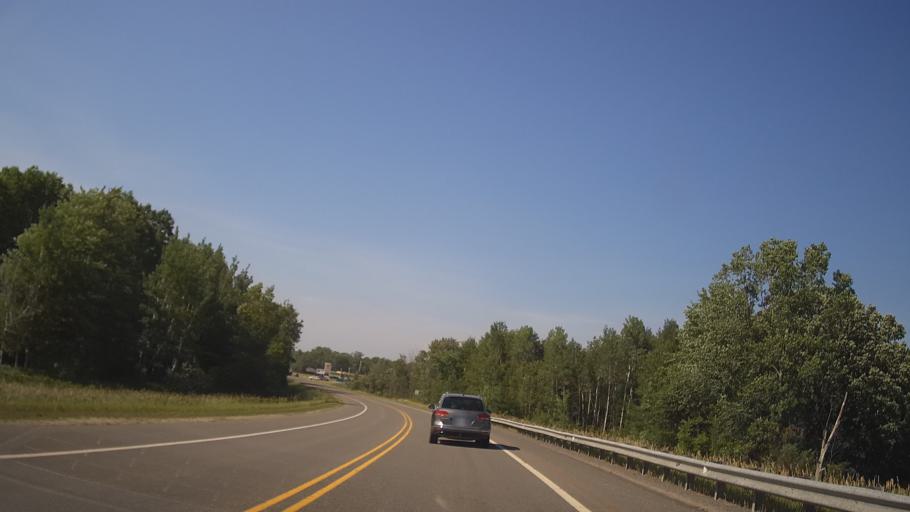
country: US
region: Michigan
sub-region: Ogemaw County
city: Skidway Lake
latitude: 44.1370
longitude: -84.1276
